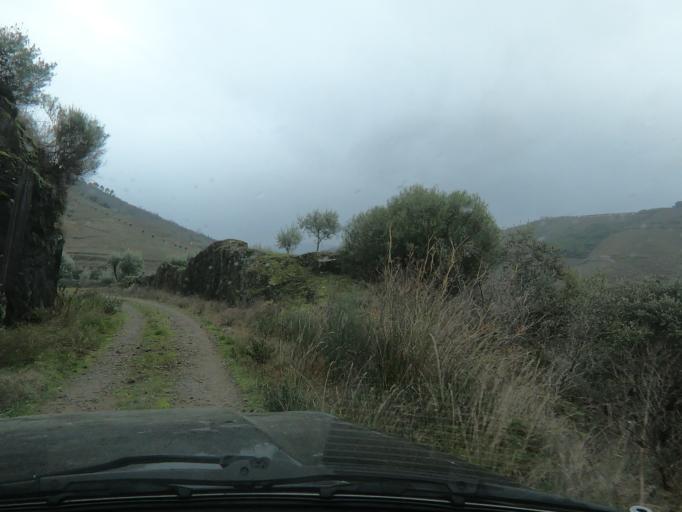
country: PT
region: Vila Real
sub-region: Santa Marta de Penaguiao
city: Santa Marta de Penaguiao
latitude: 41.2299
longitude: -7.7406
